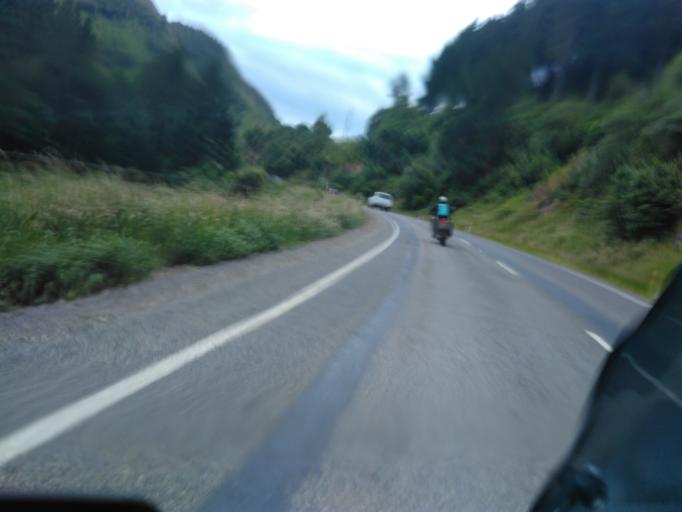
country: NZ
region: Bay of Plenty
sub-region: Opotiki District
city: Opotiki
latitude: -38.3795
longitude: 177.4783
